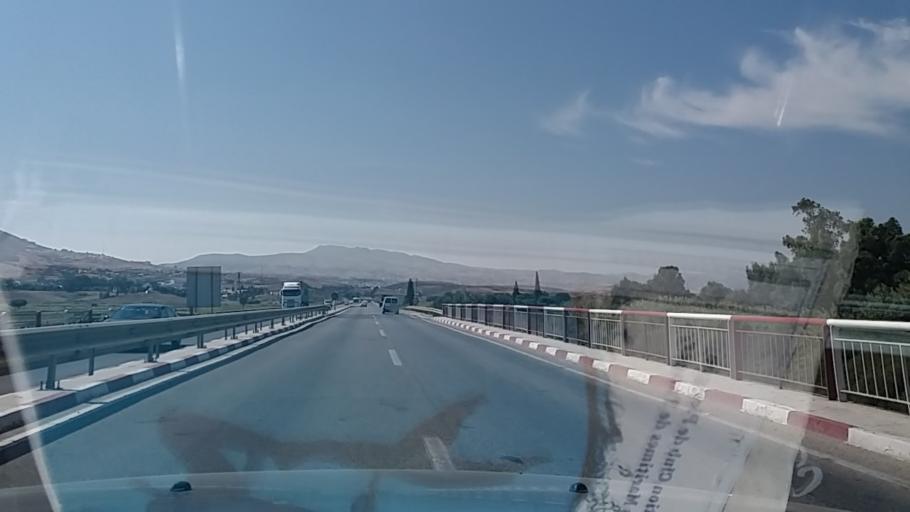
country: MA
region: Tanger-Tetouan
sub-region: Tetouan
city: Saddina
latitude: 35.5584
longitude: -5.4563
